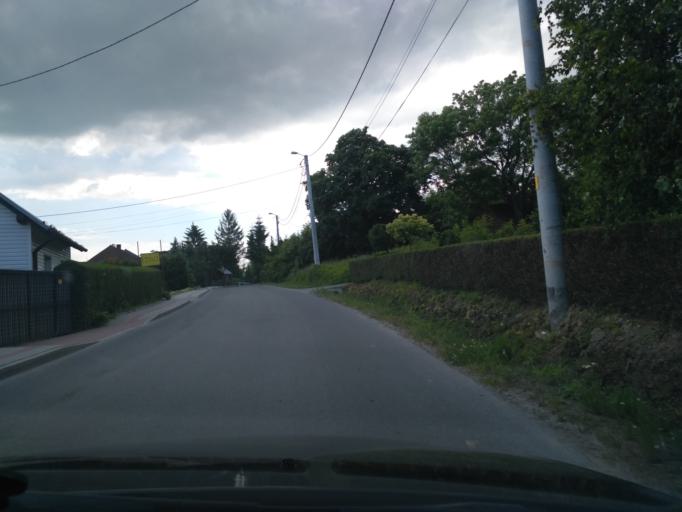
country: PL
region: Subcarpathian Voivodeship
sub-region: Powiat lancucki
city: Wysoka
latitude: 50.0509
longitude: 22.2595
